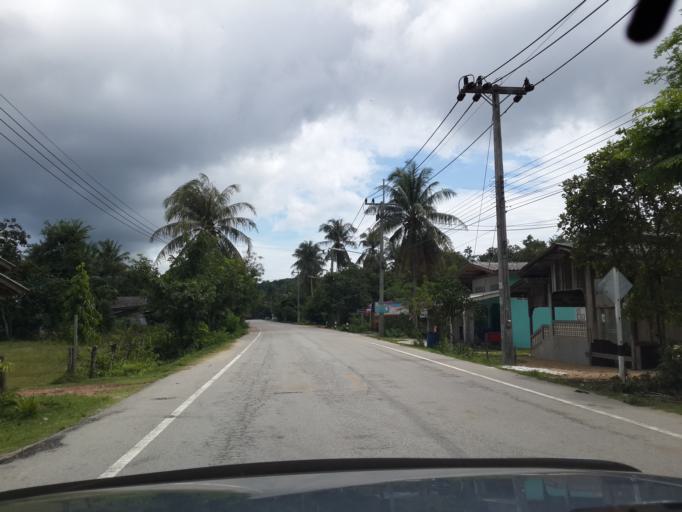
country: TH
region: Narathiwat
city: Narathiwat
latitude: 6.4746
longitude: 101.7744
